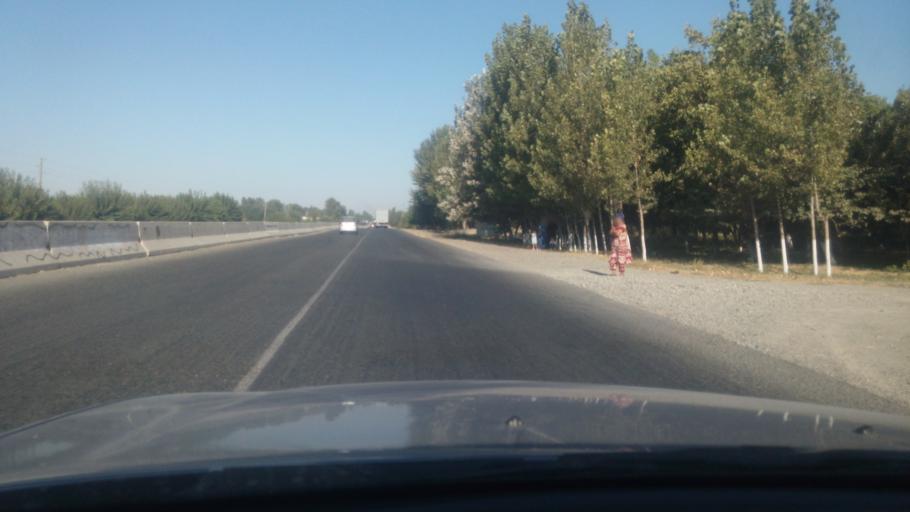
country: UZ
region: Samarqand
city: Oqtosh
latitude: 39.9440
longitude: 66.0277
